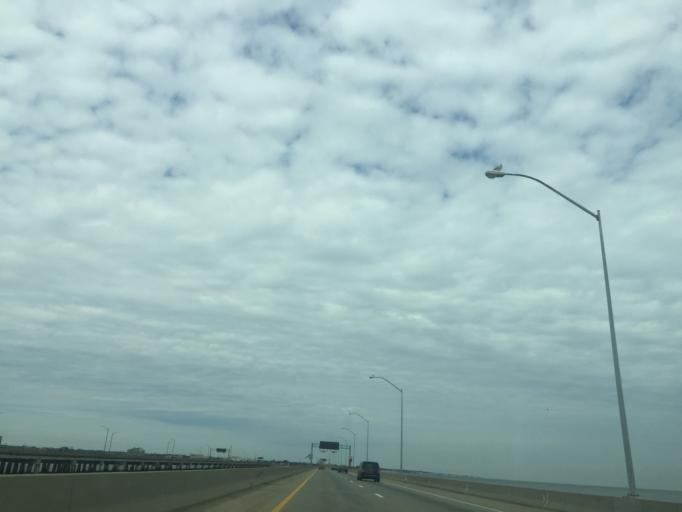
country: US
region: Virginia
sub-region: City of Hampton
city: East Hampton
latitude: 36.9730
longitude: -76.2998
